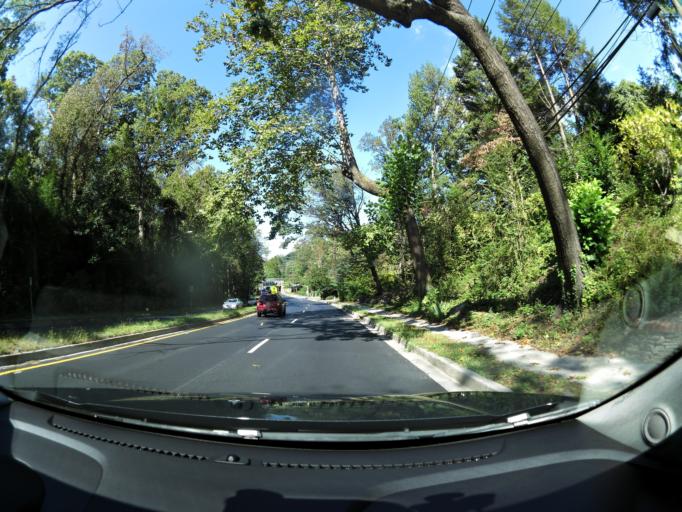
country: US
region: Maryland
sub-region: Montgomery County
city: Somerset
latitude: 38.9565
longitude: -77.1066
